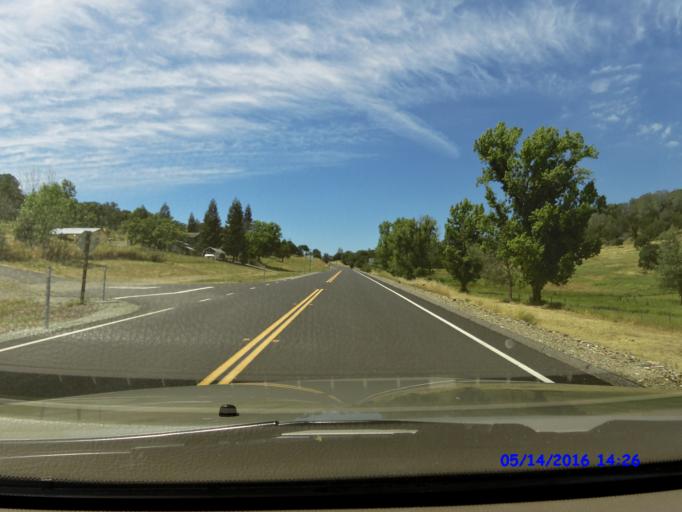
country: US
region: California
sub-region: Tuolumne County
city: Tuolumne City
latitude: 37.7129
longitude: -120.1993
